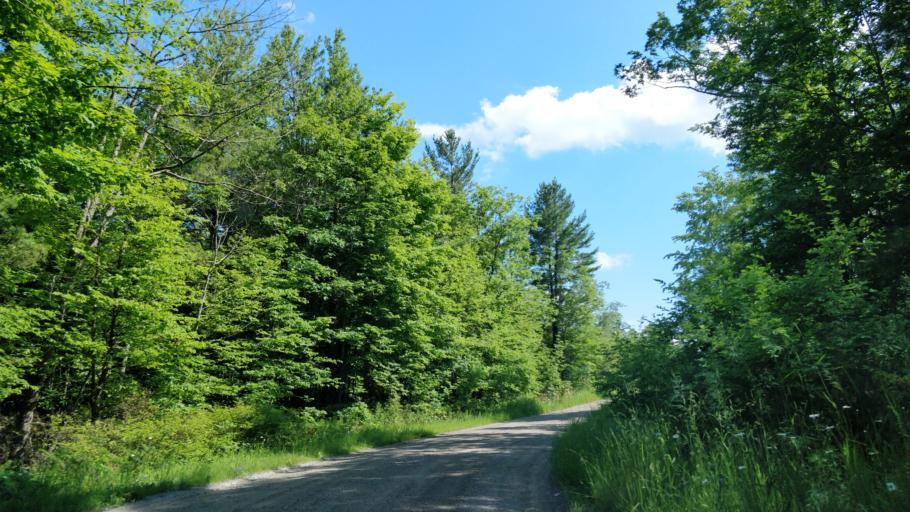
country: CA
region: Ontario
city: Perth
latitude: 44.6911
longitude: -76.5304
